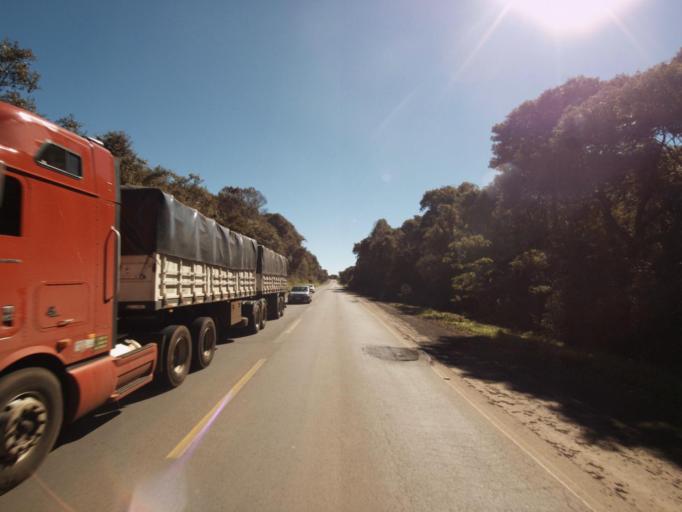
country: BR
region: Santa Catarina
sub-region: Xanxere
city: Xanxere
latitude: -26.8748
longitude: -52.1940
